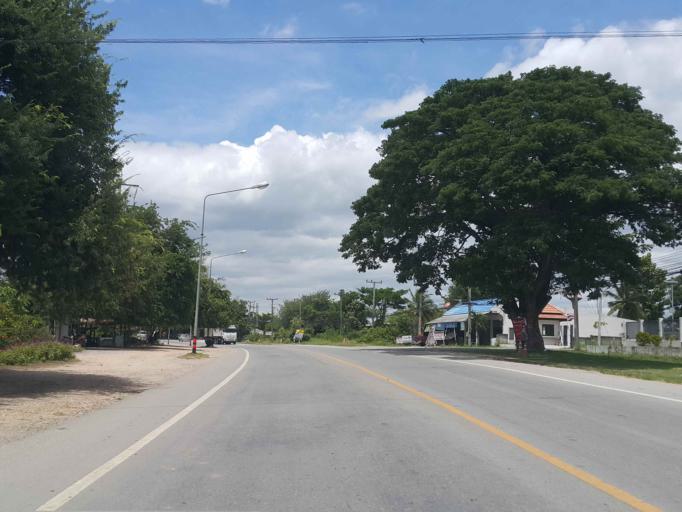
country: TH
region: Lamphun
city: Ban Hong
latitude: 18.3353
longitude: 98.8176
